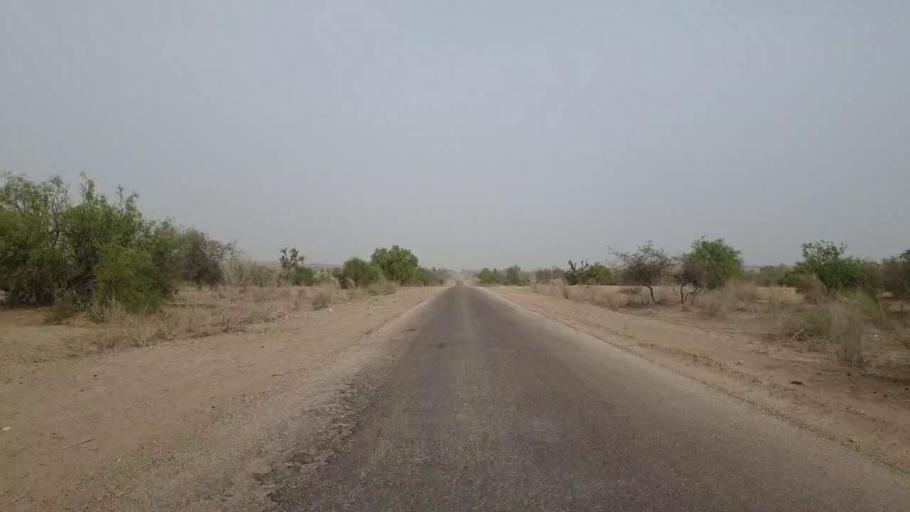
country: PK
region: Sindh
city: Islamkot
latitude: 24.5667
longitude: 70.3294
